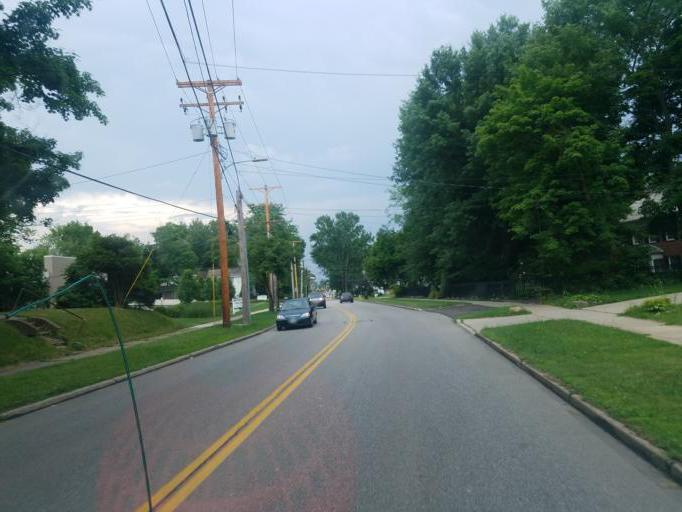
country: US
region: Ohio
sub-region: Medina County
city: Wadsworth
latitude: 41.0321
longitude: -81.7296
